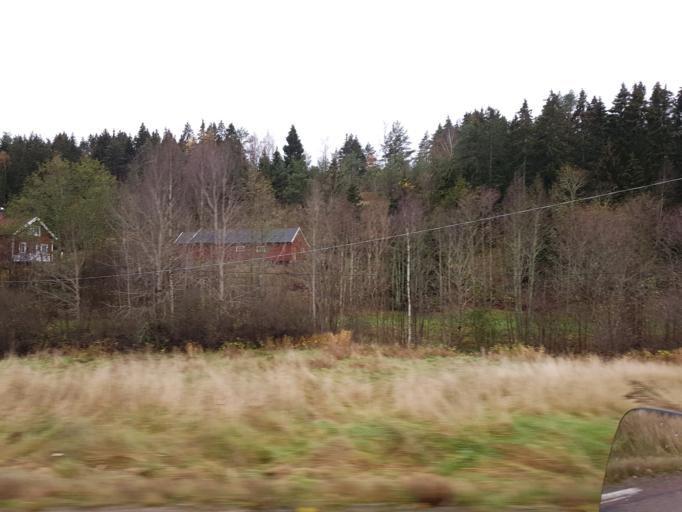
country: SE
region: Vaestra Goetaland
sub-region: Orust
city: Henan
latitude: 58.2484
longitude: 11.7886
